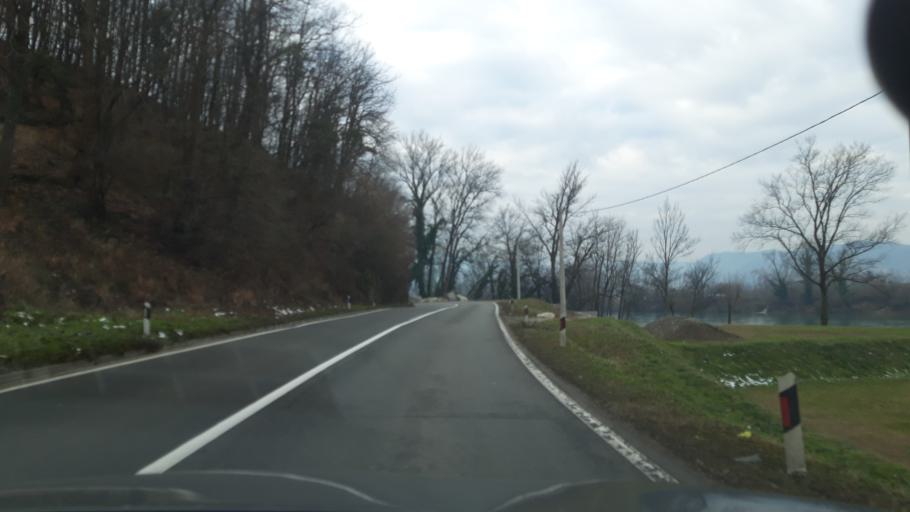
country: BA
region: Republika Srpska
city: Zvornik
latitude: 44.4214
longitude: 19.1494
